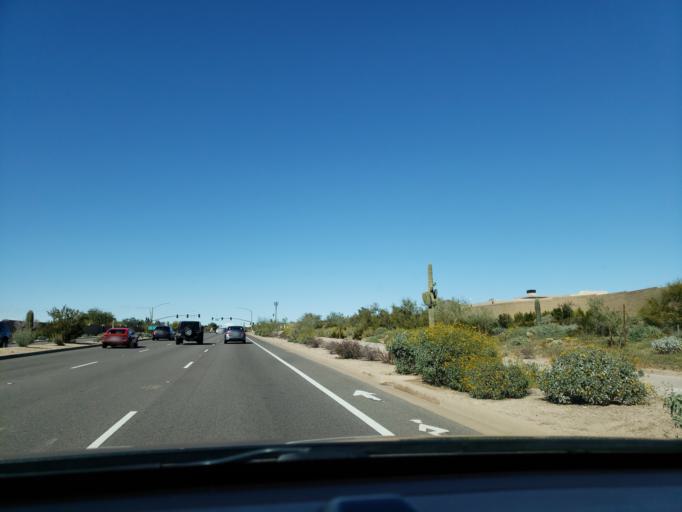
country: US
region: Arizona
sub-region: Maricopa County
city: Carefree
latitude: 33.6858
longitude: -111.8905
